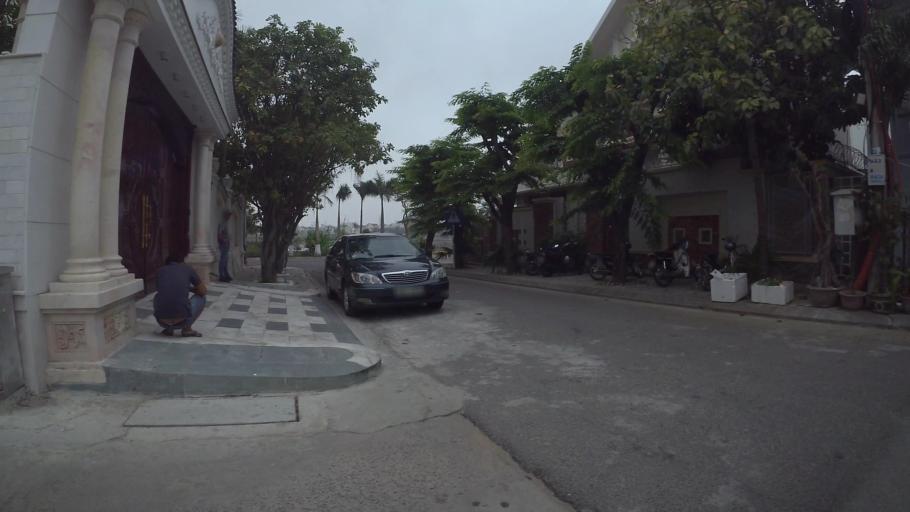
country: VN
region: Da Nang
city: Cam Le
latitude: 16.0277
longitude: 108.2238
